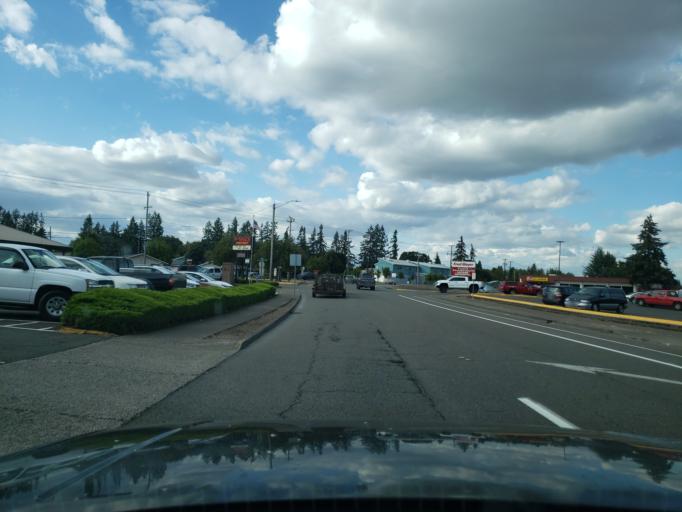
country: US
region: Oregon
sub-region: Marion County
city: Keizer
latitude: 44.9681
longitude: -123.0319
